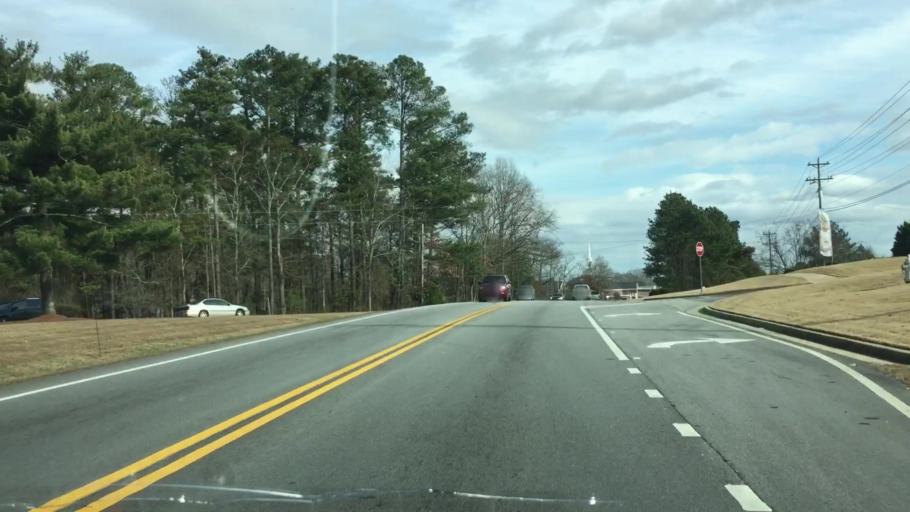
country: US
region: Georgia
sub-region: Henry County
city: McDonough
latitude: 33.4287
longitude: -84.0948
